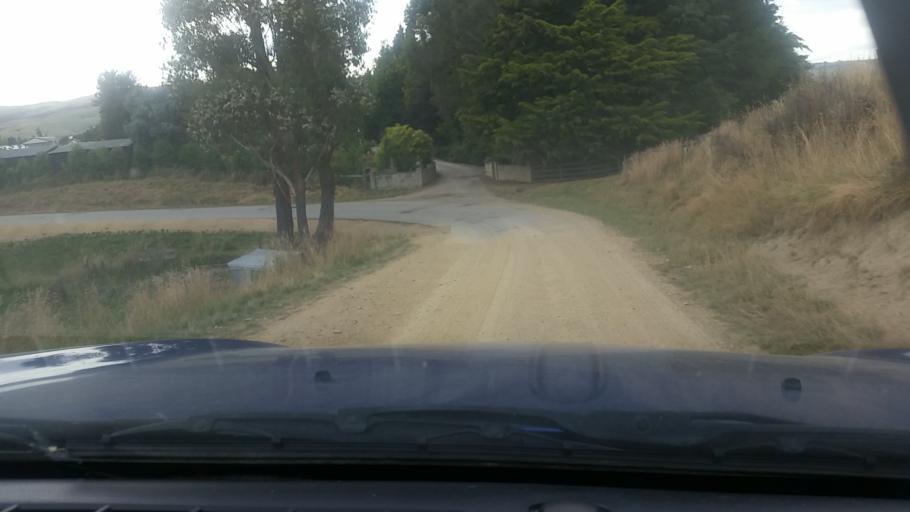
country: NZ
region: Otago
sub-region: Clutha District
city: Balclutha
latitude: -45.6807
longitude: 169.4966
